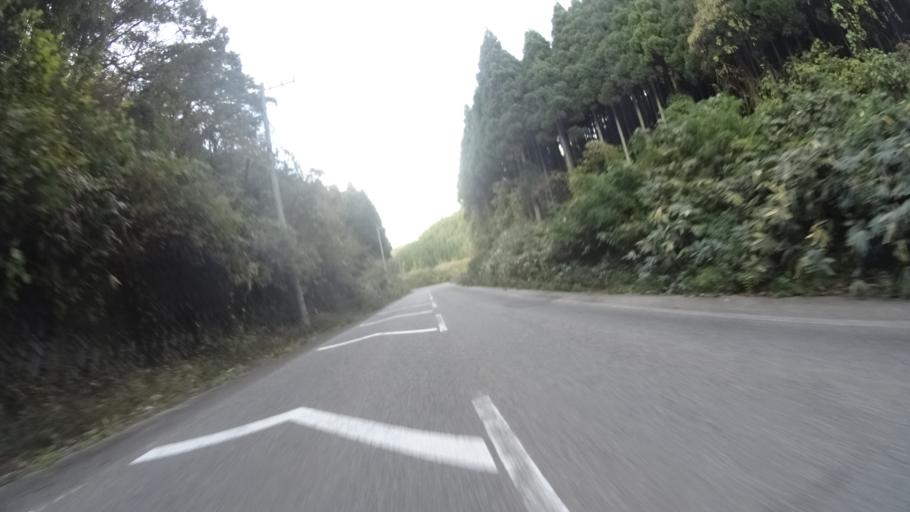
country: JP
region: Ishikawa
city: Nanao
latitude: 37.2069
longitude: 136.7078
